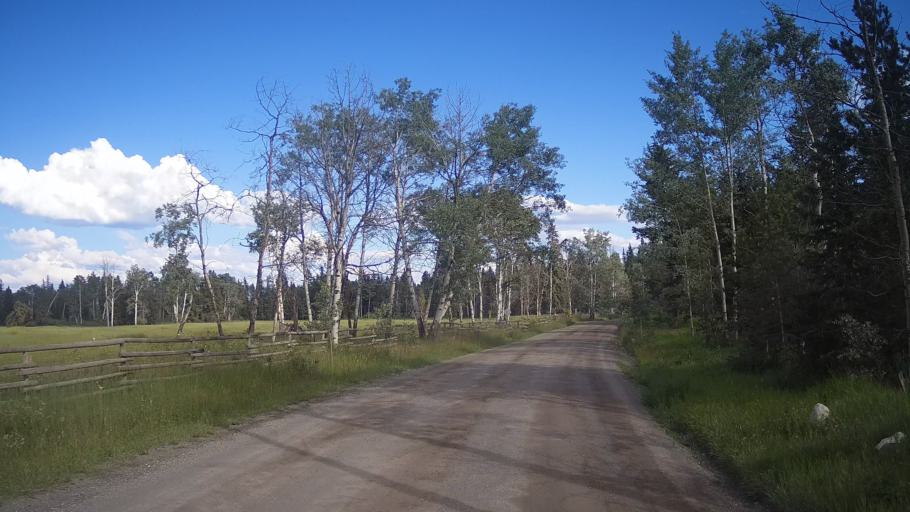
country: CA
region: British Columbia
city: Cache Creek
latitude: 51.1794
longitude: -121.5780
